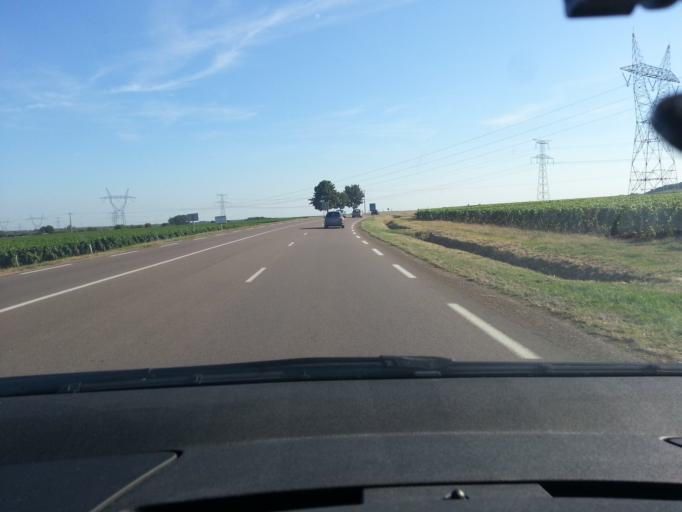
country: FR
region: Bourgogne
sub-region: Departement de la Cote-d'Or
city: Nuits-Saint-Georges
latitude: 47.1258
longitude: 4.9445
